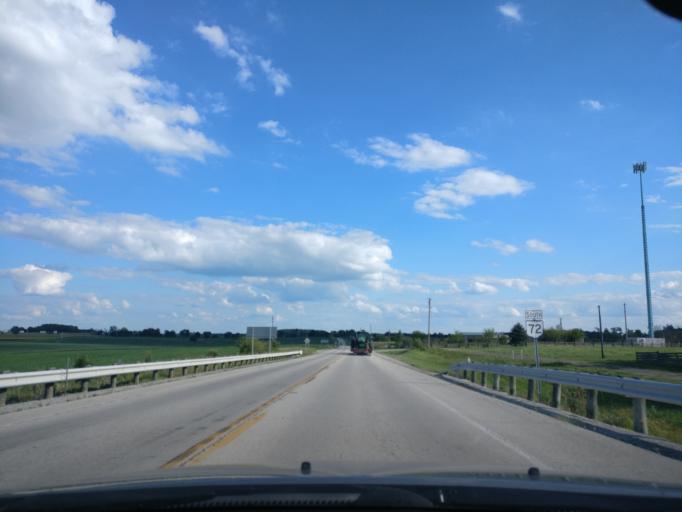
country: US
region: Ohio
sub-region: Greene County
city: Jamestown
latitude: 39.5558
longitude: -83.7184
